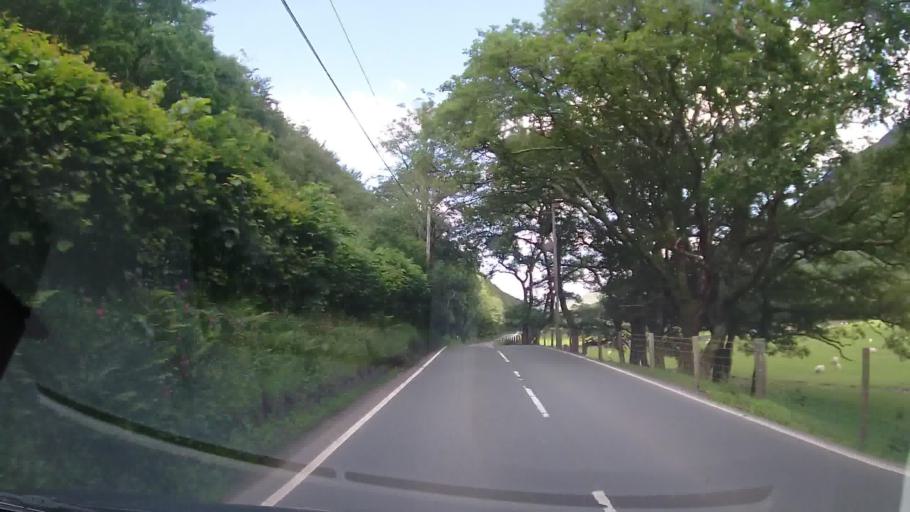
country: GB
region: Wales
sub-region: Gwynedd
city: Corris
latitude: 52.6596
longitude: -3.9269
